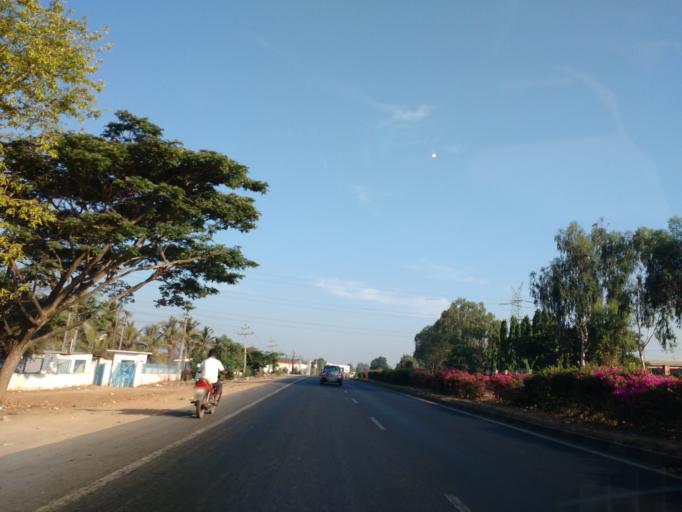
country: IN
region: Karnataka
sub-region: Bangalore Rural
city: Nelamangala
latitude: 13.1319
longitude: 77.3580
